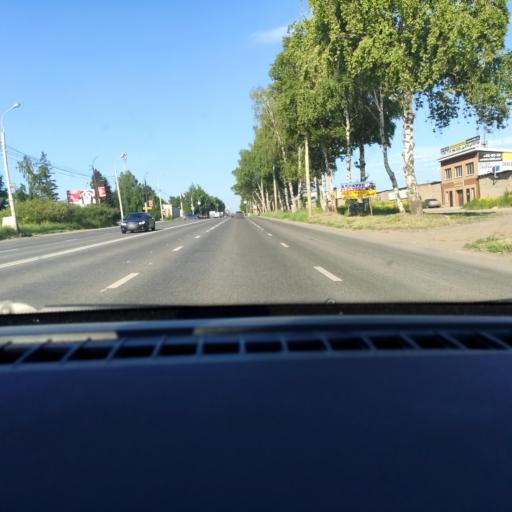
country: RU
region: Udmurtiya
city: Khokhryaki
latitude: 56.9032
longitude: 53.3298
